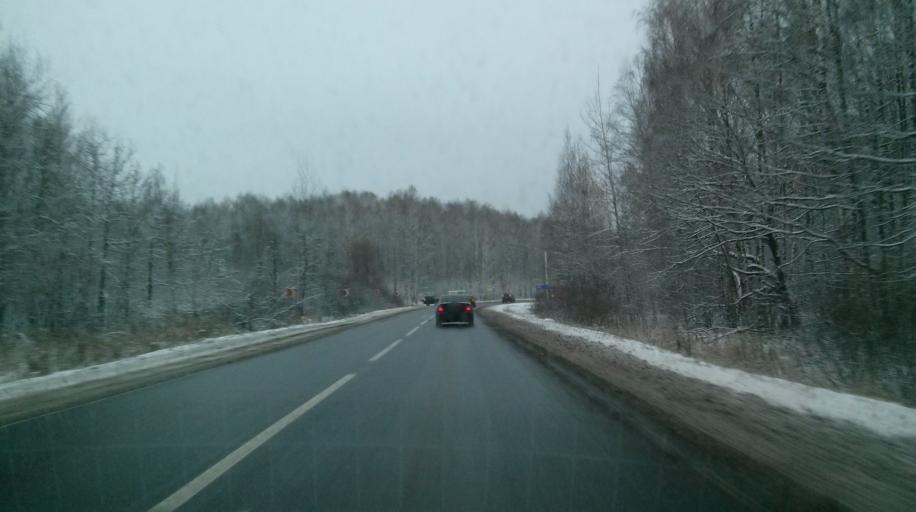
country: RU
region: Nizjnij Novgorod
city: Vorsma
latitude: 56.0142
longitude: 43.3444
